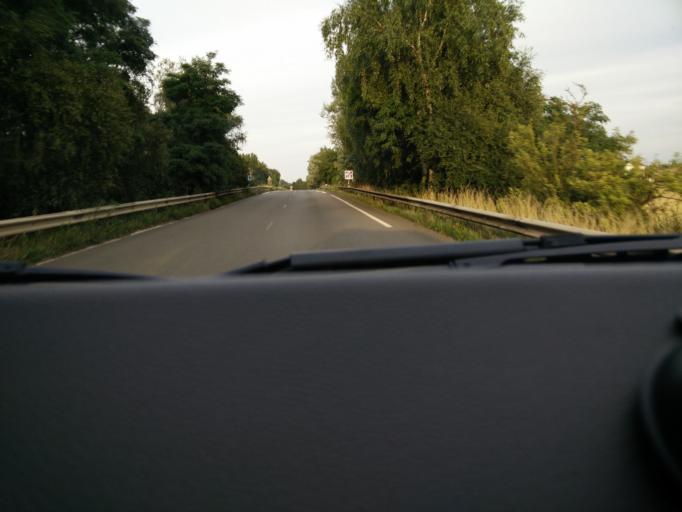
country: FR
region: Nord-Pas-de-Calais
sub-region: Departement du Nord
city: Marly
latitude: 50.3336
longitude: 3.5551
